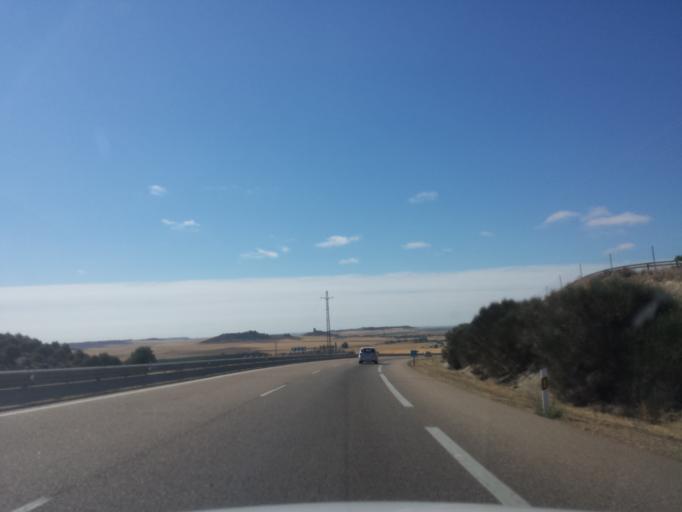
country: ES
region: Castille and Leon
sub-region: Provincia de Valladolid
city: Mota del Marques
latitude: 41.6700
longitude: -5.1987
